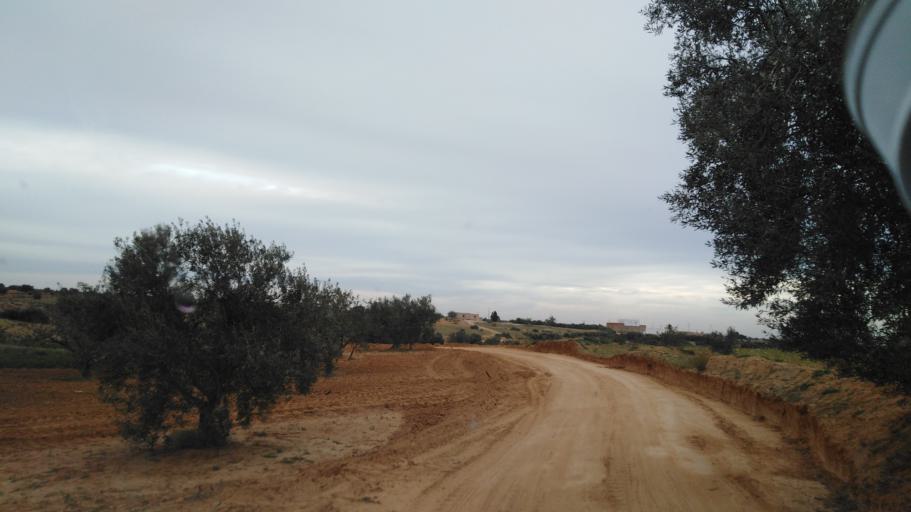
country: TN
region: Safaqis
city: Bi'r `Ali Bin Khalifah
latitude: 34.7681
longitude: 10.3750
